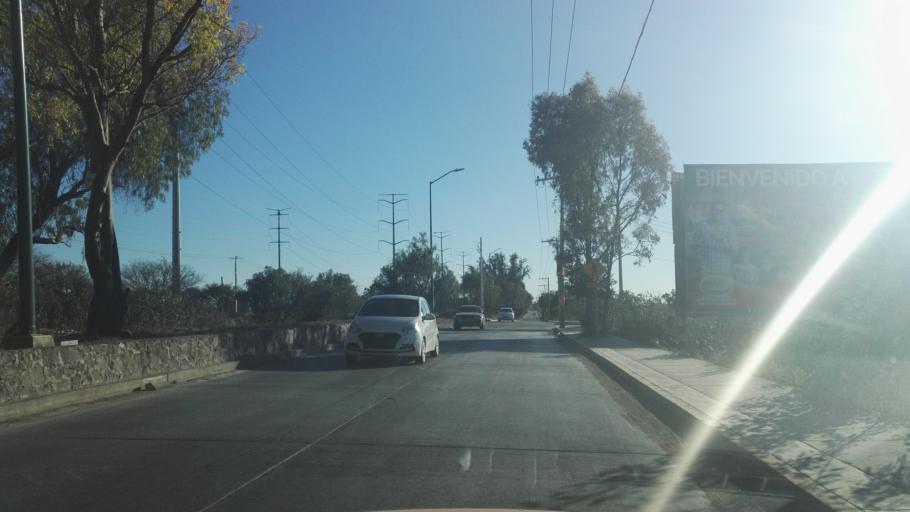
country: MX
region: Guanajuato
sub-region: Leon
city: Fraccionamiento Paraiso Real
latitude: 21.0642
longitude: -101.6062
